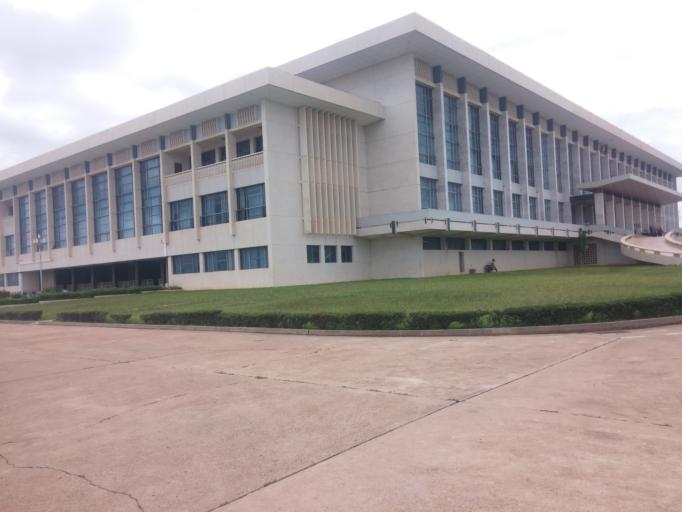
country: TG
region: Kara
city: Kara
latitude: 9.5597
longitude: 1.1810
